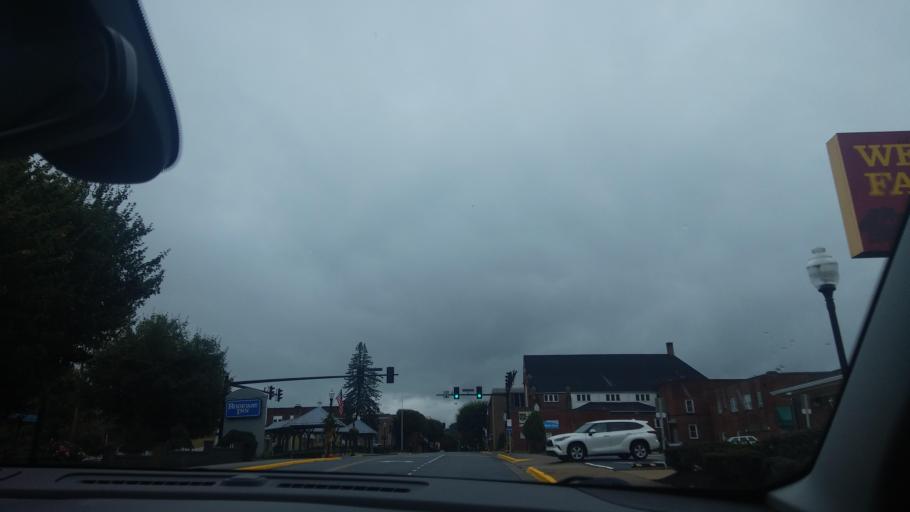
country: US
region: Virginia
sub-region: City of Galax
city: Galax
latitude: 36.6642
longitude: -80.9258
